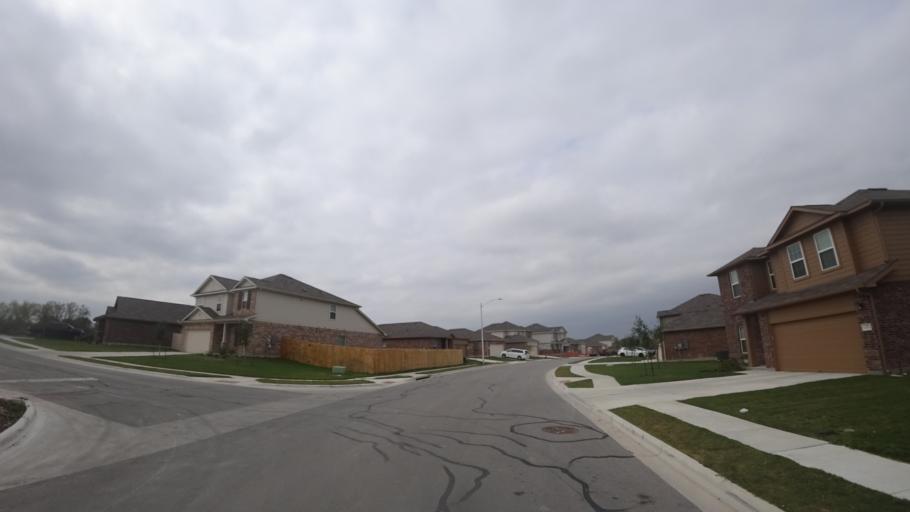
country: US
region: Texas
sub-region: Travis County
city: Pflugerville
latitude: 30.3918
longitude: -97.6194
